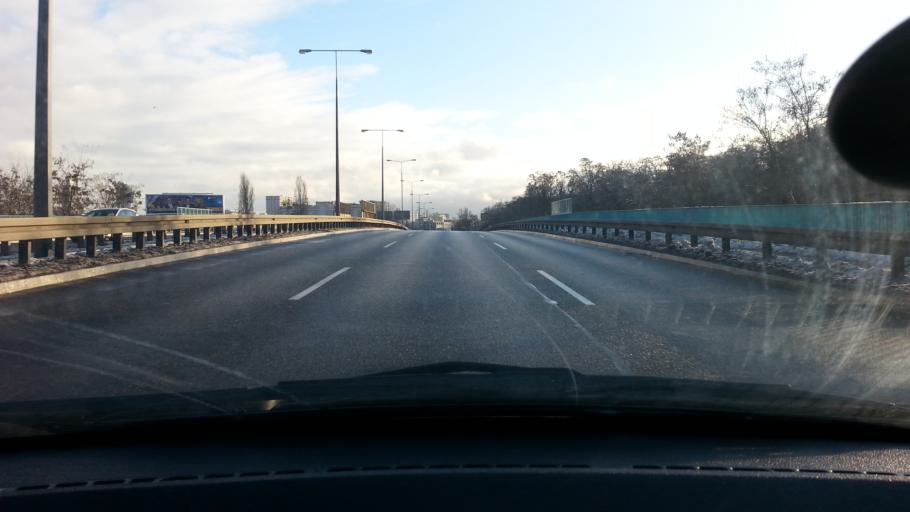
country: PL
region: Masovian Voivodeship
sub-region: Warszawa
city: Zoliborz
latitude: 52.2534
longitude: 20.9543
